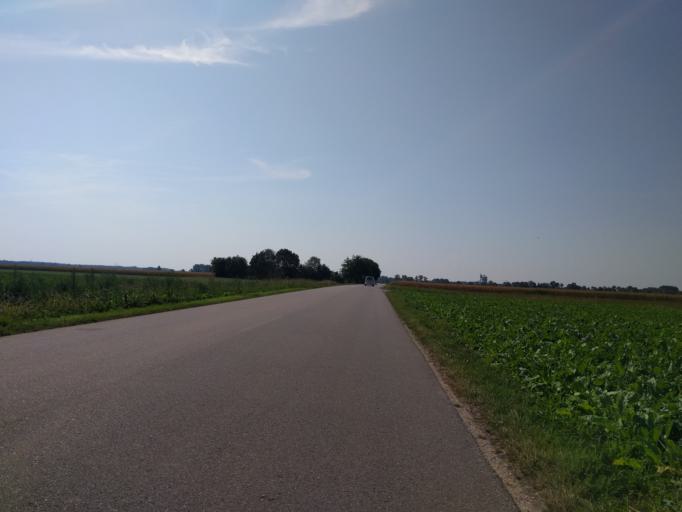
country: DE
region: Bavaria
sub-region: Upper Palatinate
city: Donaustauf
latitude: 49.0123
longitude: 12.2350
